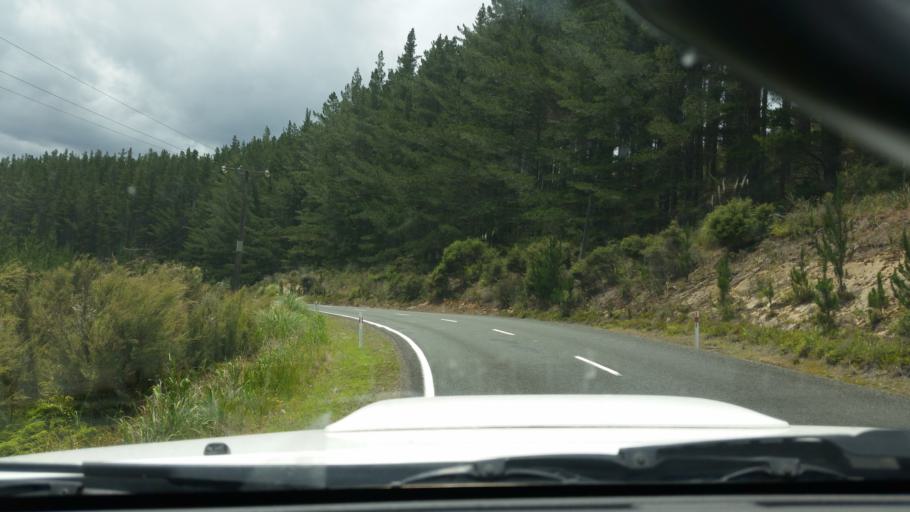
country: NZ
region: Northland
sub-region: Kaipara District
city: Dargaville
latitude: -35.8221
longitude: 173.7088
